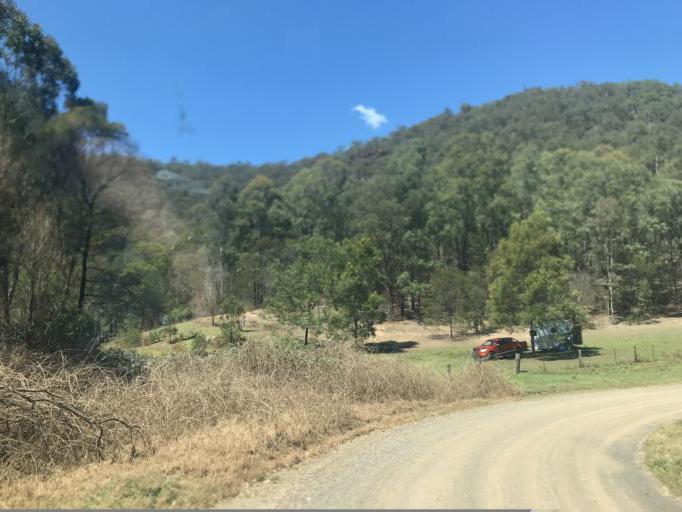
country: AU
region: New South Wales
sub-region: Hornsby Shire
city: Glenorie
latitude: -33.2576
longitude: 150.9754
